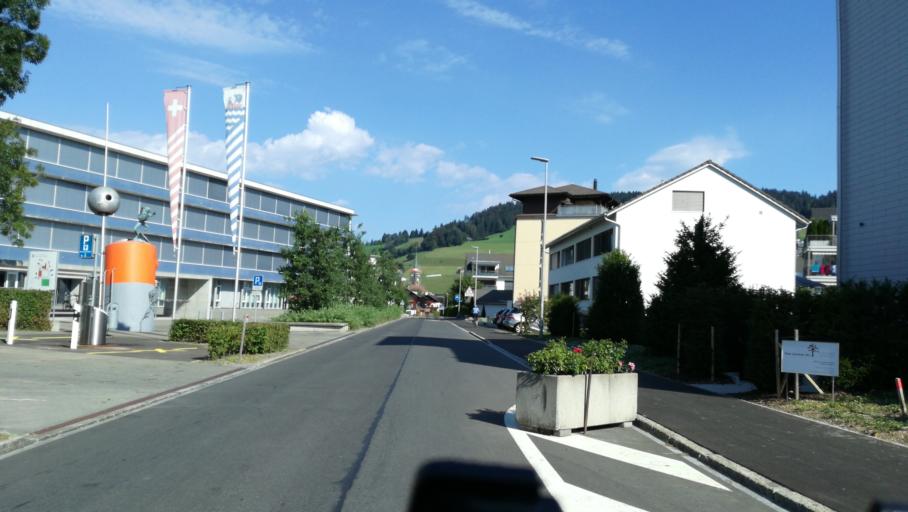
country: CH
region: Zug
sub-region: Zug
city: Unterageri
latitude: 47.1320
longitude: 8.5872
